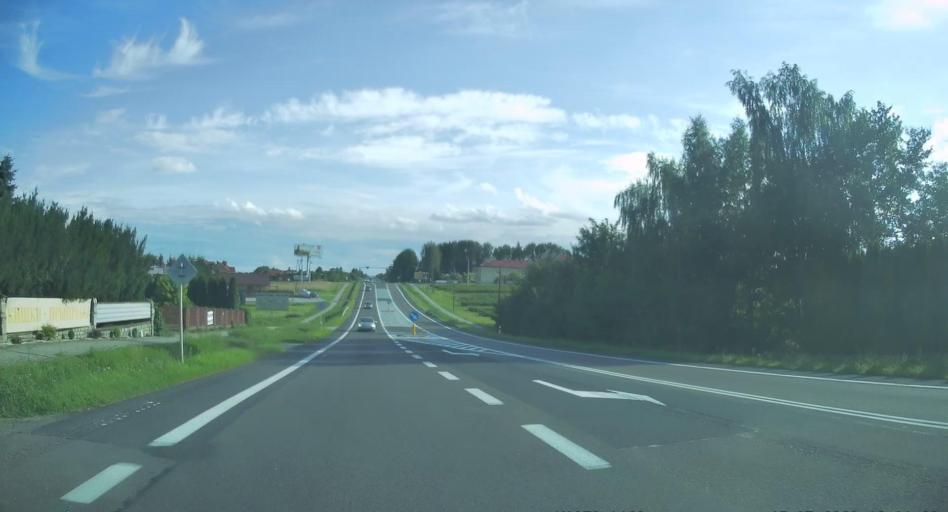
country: PL
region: Subcarpathian Voivodeship
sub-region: Powiat przemyski
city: Orly
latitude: 49.8713
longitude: 22.8111
